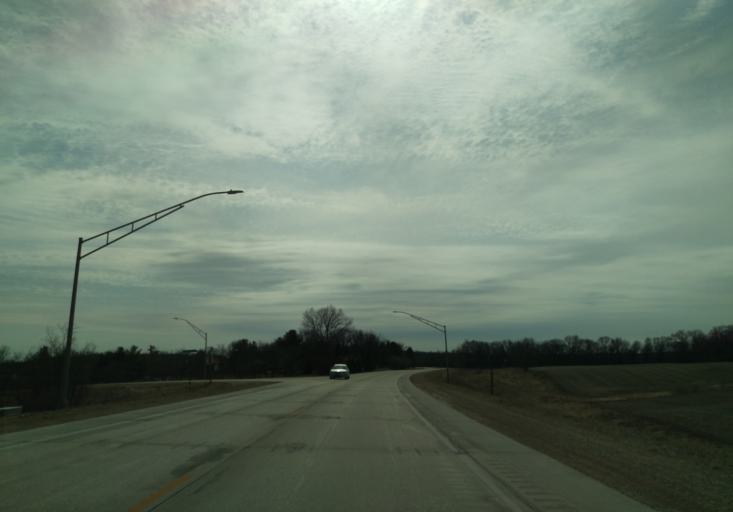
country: US
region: Iowa
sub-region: Winneshiek County
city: Decorah
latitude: 43.3457
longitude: -91.8068
